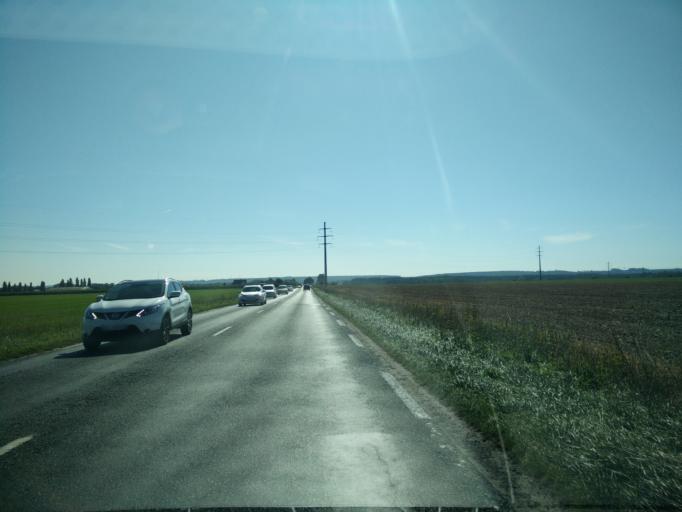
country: FR
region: Ile-de-France
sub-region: Departement de Seine-et-Marne
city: Claye-Souilly
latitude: 48.9746
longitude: 2.6609
